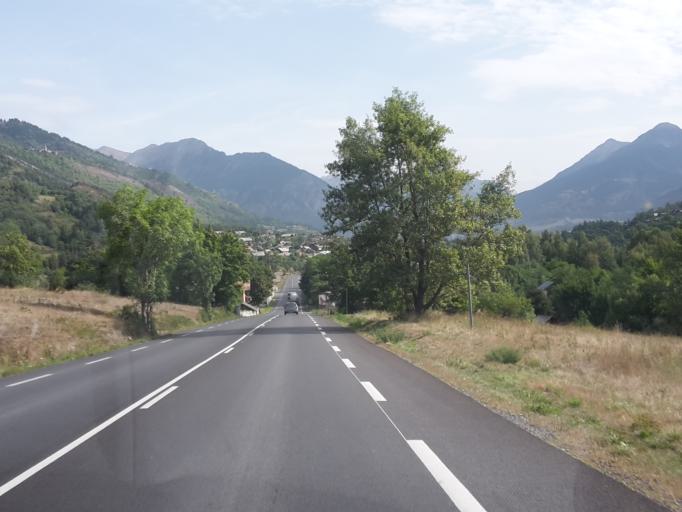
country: FR
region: Provence-Alpes-Cote d'Azur
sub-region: Departement des Hautes-Alpes
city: Saint-Martin-de-Queyrieres
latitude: 44.8562
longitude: 6.5860
